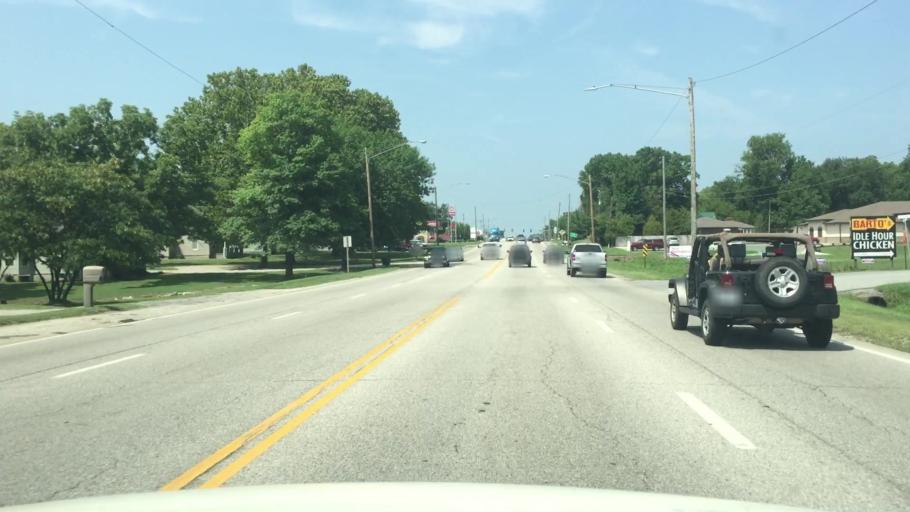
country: US
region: Kansas
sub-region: Crawford County
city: Frontenac
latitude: 37.4512
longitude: -94.7051
